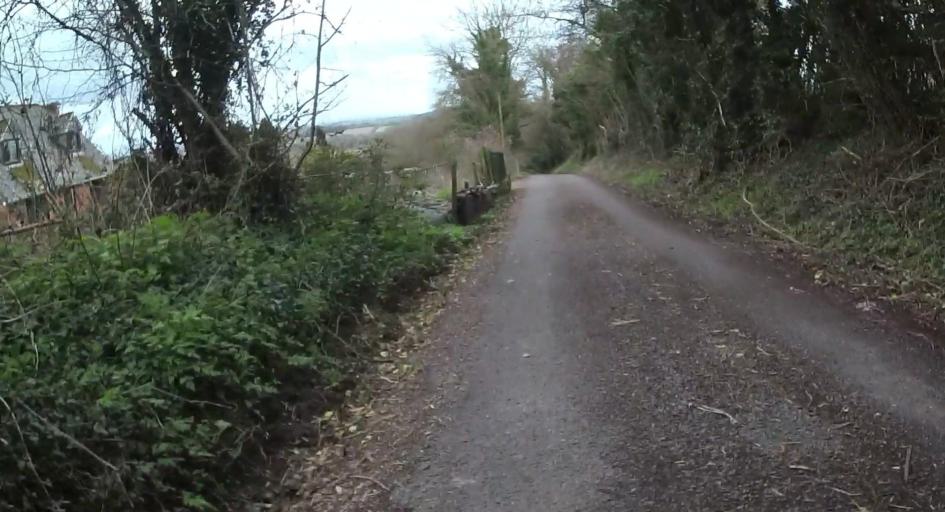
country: GB
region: England
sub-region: Hampshire
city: Alton
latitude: 51.1670
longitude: -0.9739
